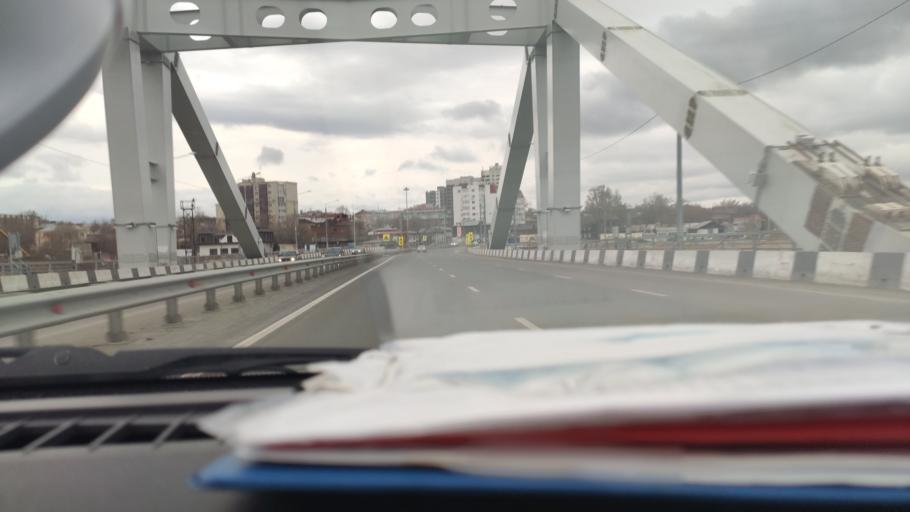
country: RU
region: Samara
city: Rozhdestveno
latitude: 53.1766
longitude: 50.0865
